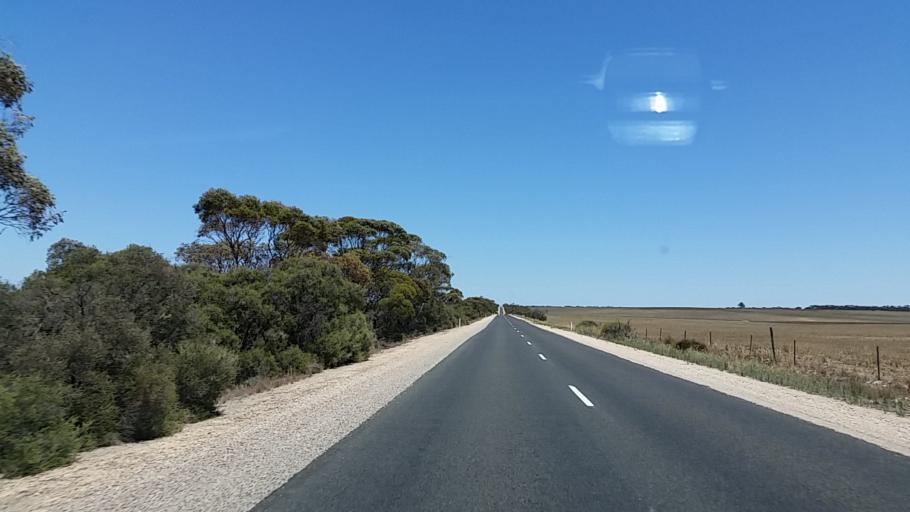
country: AU
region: South Australia
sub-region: Mid Murray
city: Mannum
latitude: -34.7572
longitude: 139.5084
